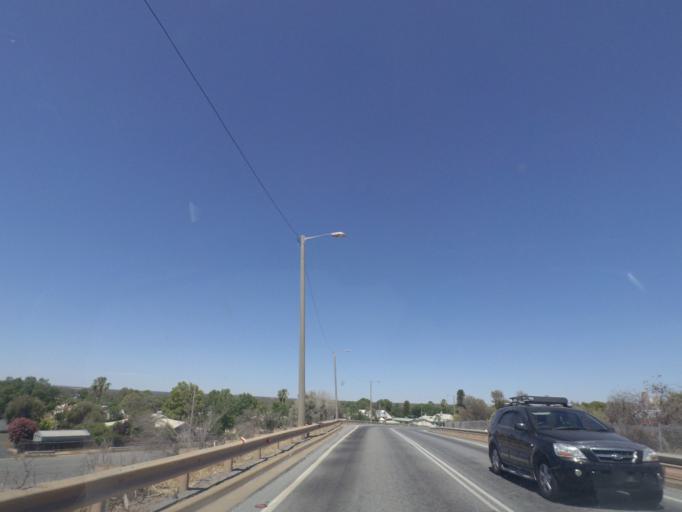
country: AU
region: New South Wales
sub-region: Narrandera
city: Narrandera
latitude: -34.7408
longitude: 146.5594
